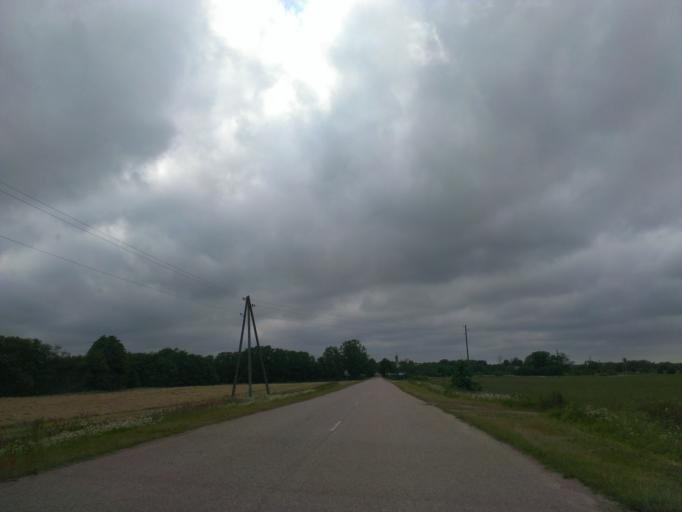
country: LV
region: Durbe
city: Liegi
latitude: 56.7285
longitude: 21.4075
